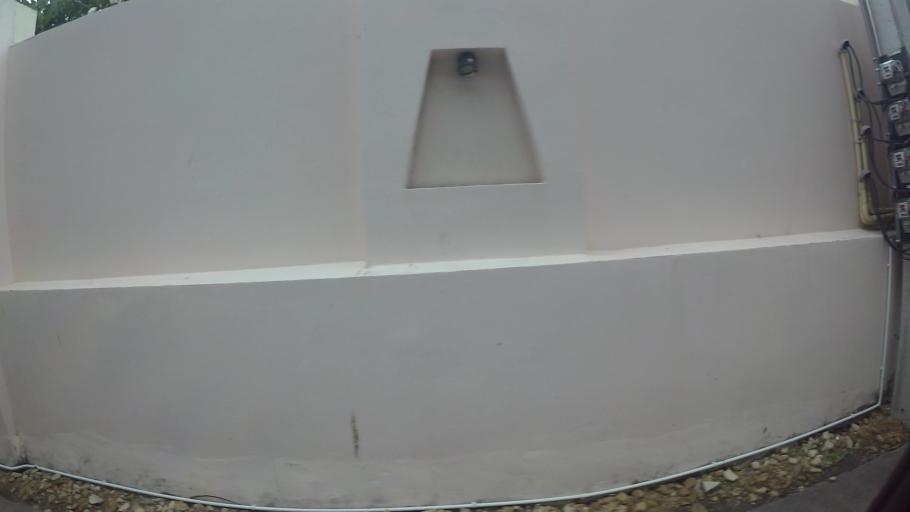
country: TH
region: Chon Buri
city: Sattahip
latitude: 12.7655
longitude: 100.8935
